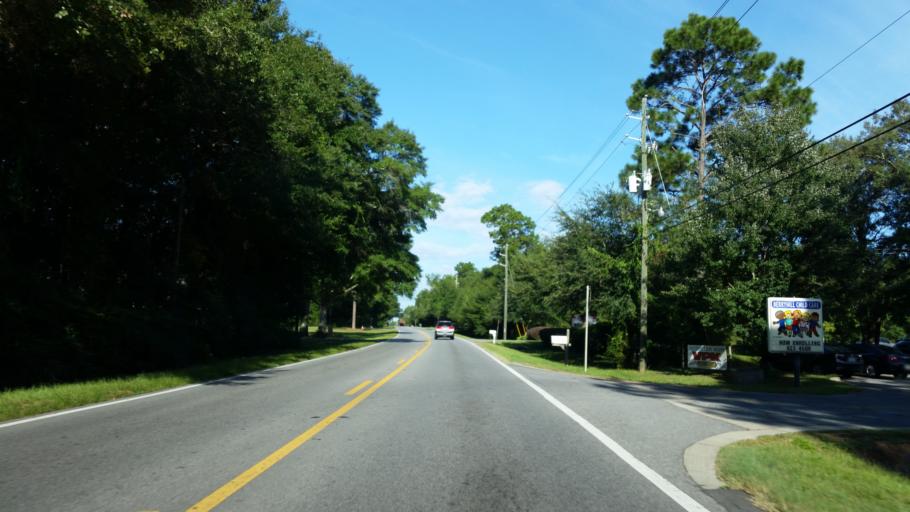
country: US
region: Florida
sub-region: Santa Rosa County
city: Milton
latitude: 30.6374
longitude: -87.0779
